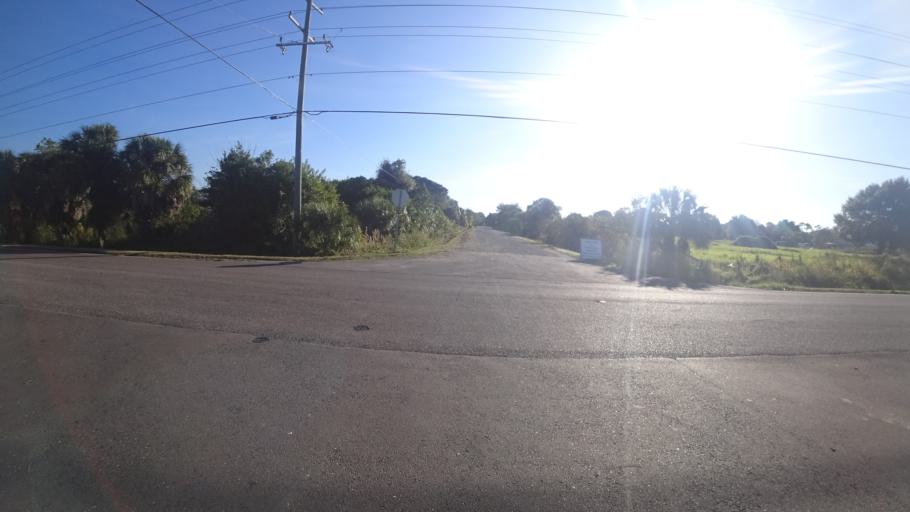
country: US
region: Florida
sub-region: Manatee County
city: Memphis
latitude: 27.5682
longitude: -82.5278
